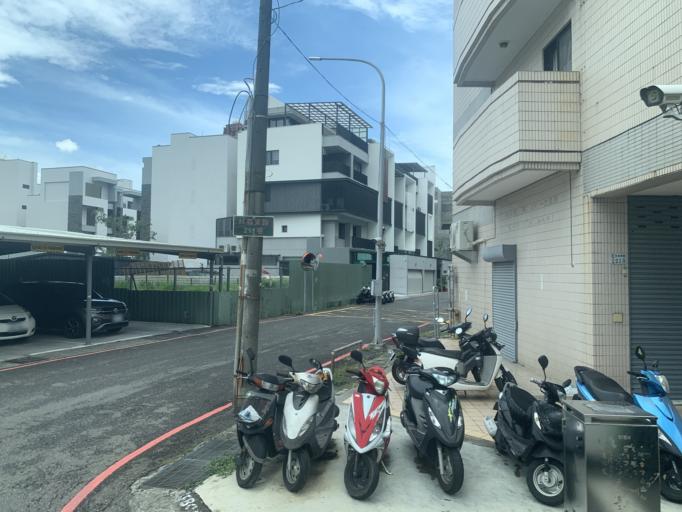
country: TW
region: Taiwan
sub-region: Chiayi
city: Jiayi Shi
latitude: 23.4884
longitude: 120.4624
